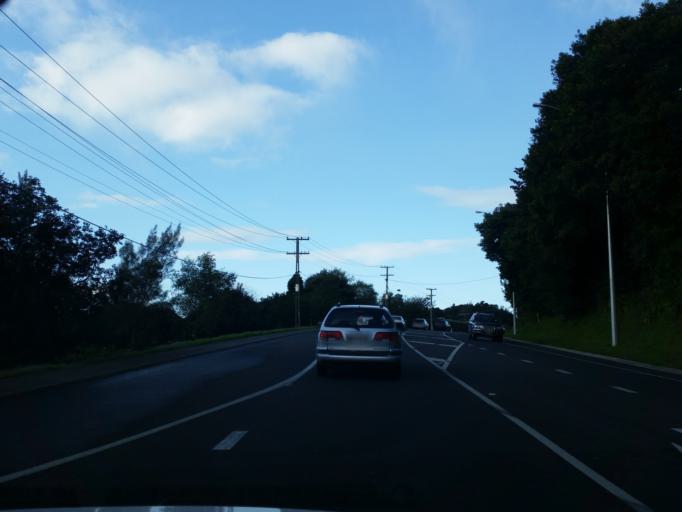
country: NZ
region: Bay of Plenty
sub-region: Tauranga City
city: Tauranga
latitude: -37.6958
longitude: 176.1007
